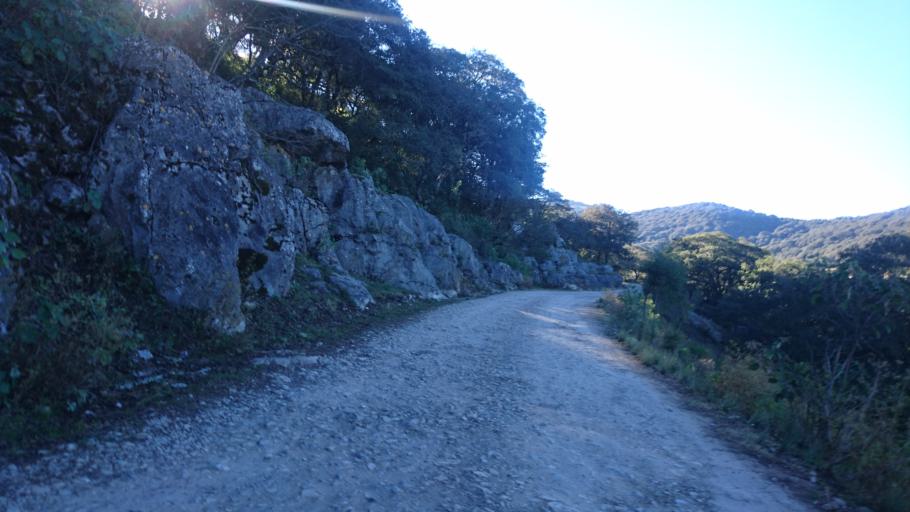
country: MX
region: San Luis Potosi
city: Zaragoza
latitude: 22.0307
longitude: -100.6070
